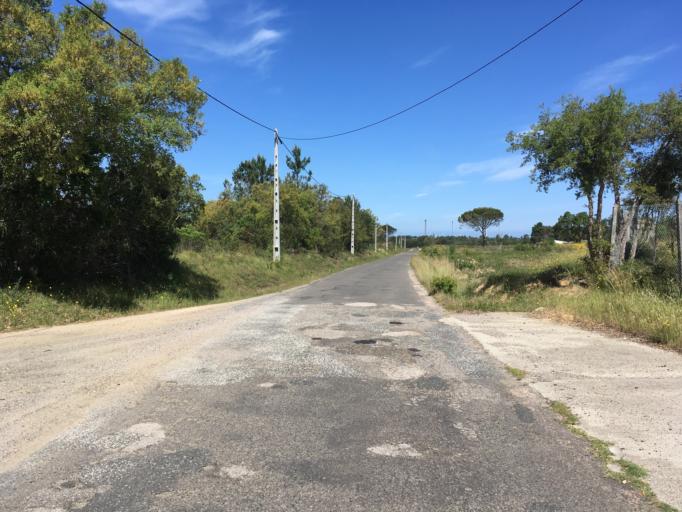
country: PT
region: Setubal
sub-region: Sines
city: Porto Covo
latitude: 37.9382
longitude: -8.7702
